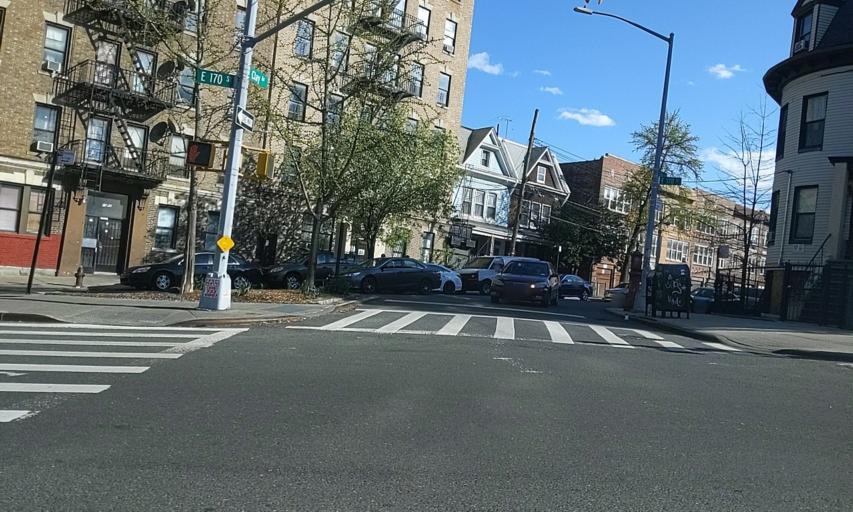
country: US
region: New York
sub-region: New York County
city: Inwood
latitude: 40.8372
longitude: -73.9081
